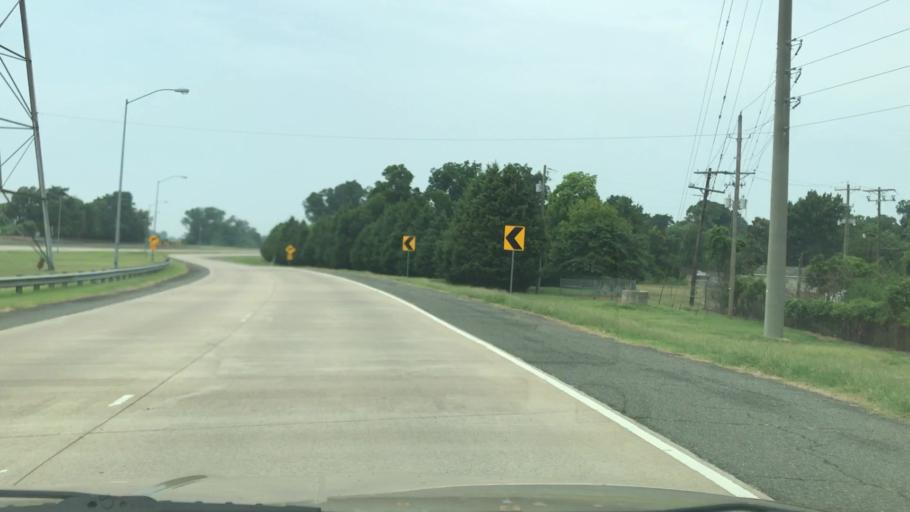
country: US
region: Louisiana
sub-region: Bossier Parish
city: Bossier City
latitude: 32.5037
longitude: -93.7076
